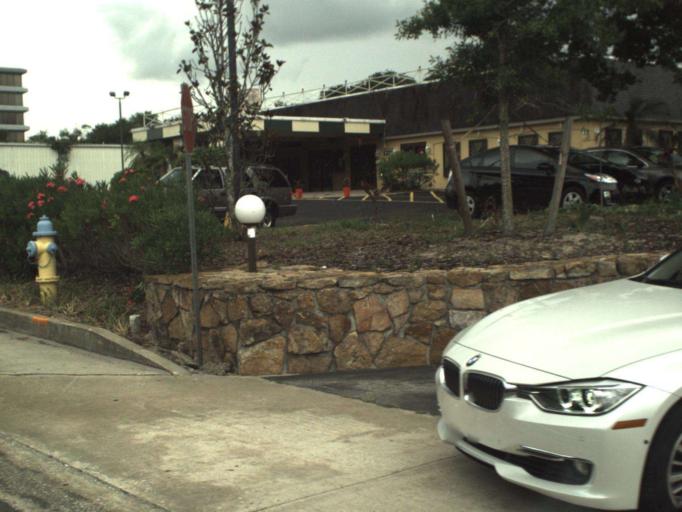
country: US
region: Florida
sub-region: Seminole County
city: Altamonte Springs
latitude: 28.6630
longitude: -81.3632
